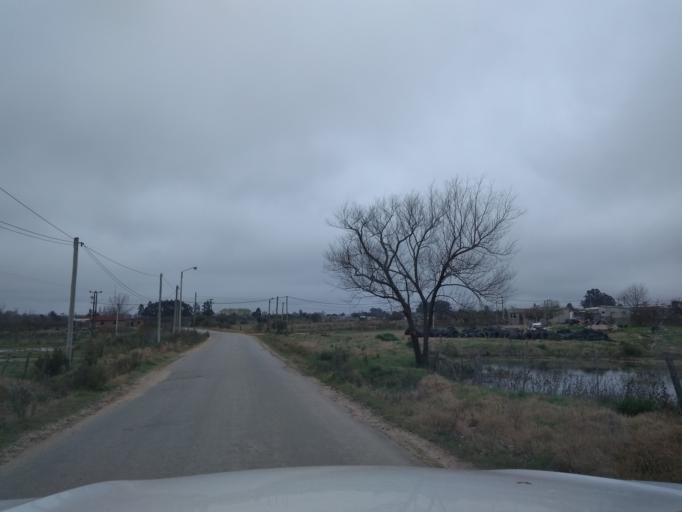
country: UY
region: Florida
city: Florida
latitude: -34.0810
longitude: -56.2037
